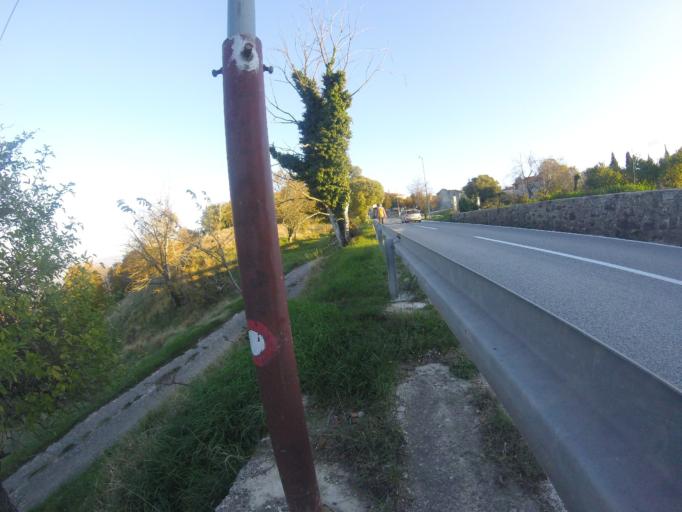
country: HR
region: Istarska
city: Pazin
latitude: 45.2215
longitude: 14.0076
